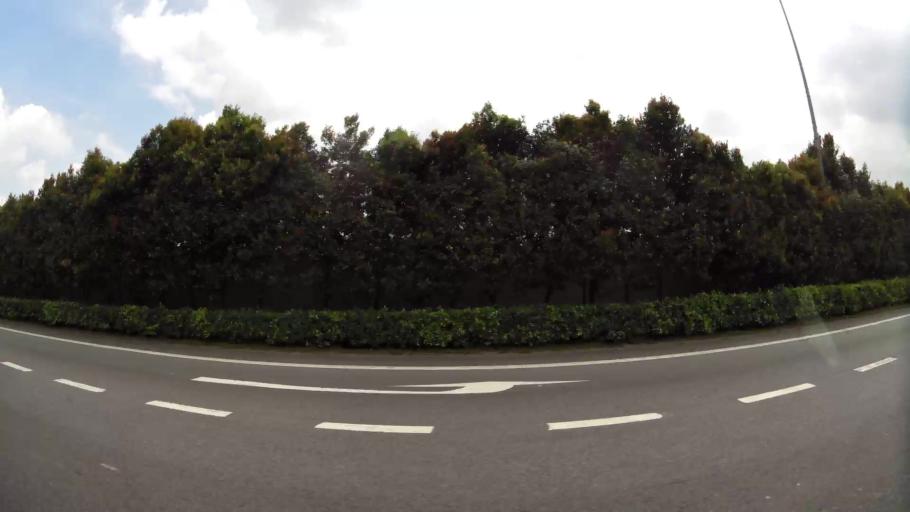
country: SG
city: Singapore
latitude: 1.3805
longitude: 103.8585
